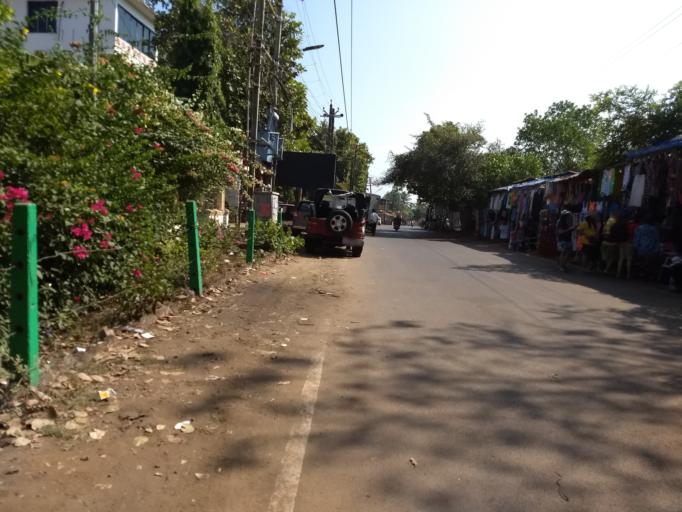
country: IN
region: Goa
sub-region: North Goa
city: Vagator
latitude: 15.5990
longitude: 73.7420
